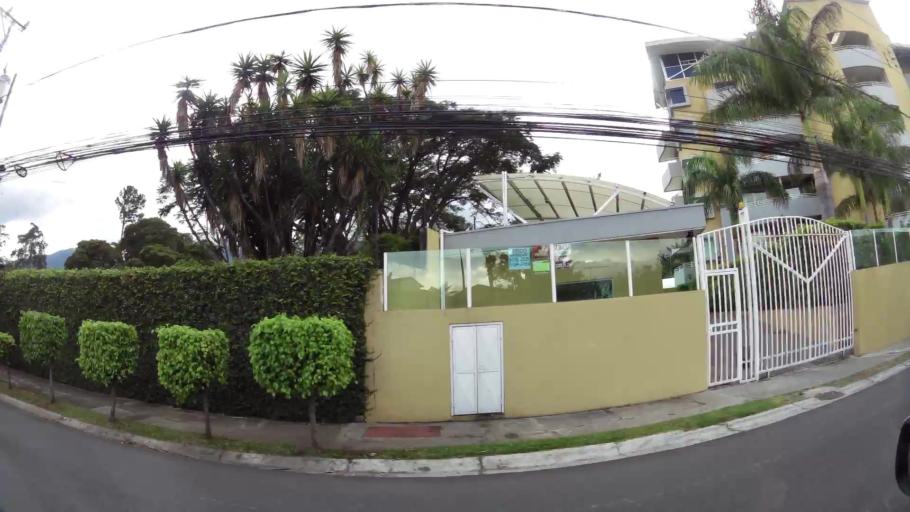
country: CR
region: San Jose
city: San Rafael
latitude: 9.9287
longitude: -84.1492
